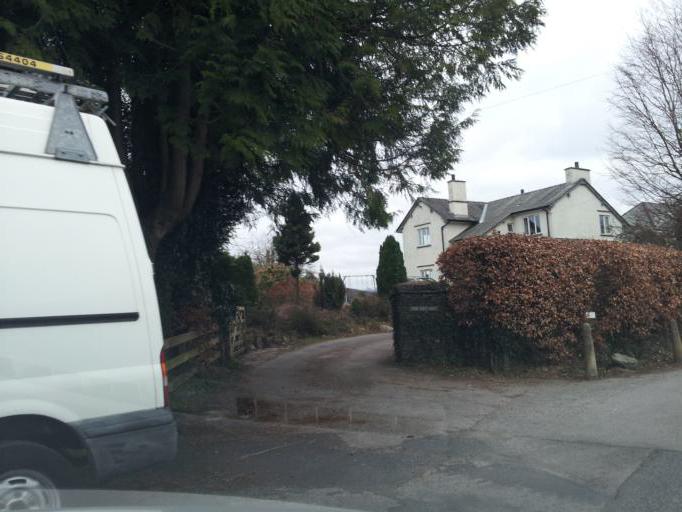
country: GB
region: England
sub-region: Cumbria
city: Windermere
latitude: 54.3672
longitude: -2.9176
